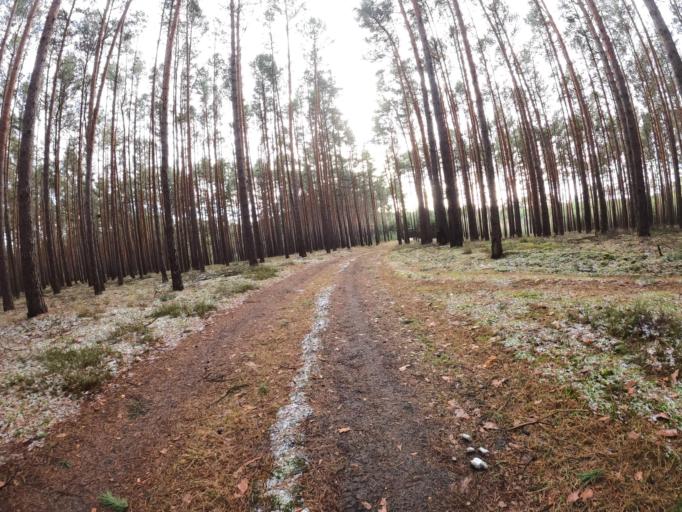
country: PL
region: Lubusz
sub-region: Powiat slubicki
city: Cybinka
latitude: 52.2519
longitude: 14.7975
